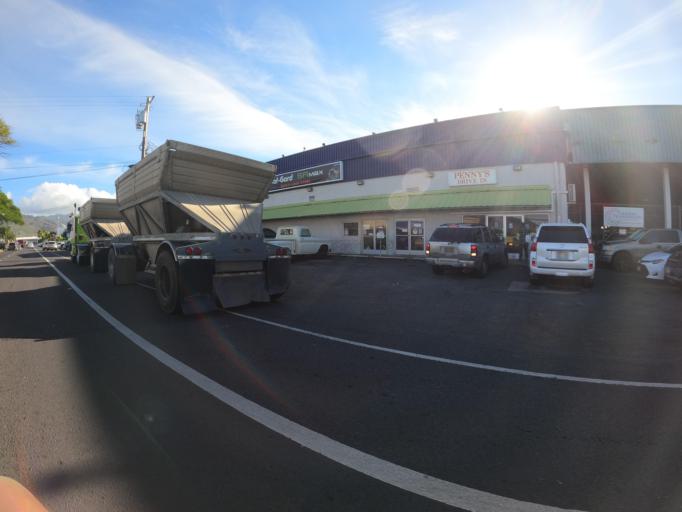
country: US
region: Hawaii
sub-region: Honolulu County
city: Honolulu
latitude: 21.3256
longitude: -157.8891
